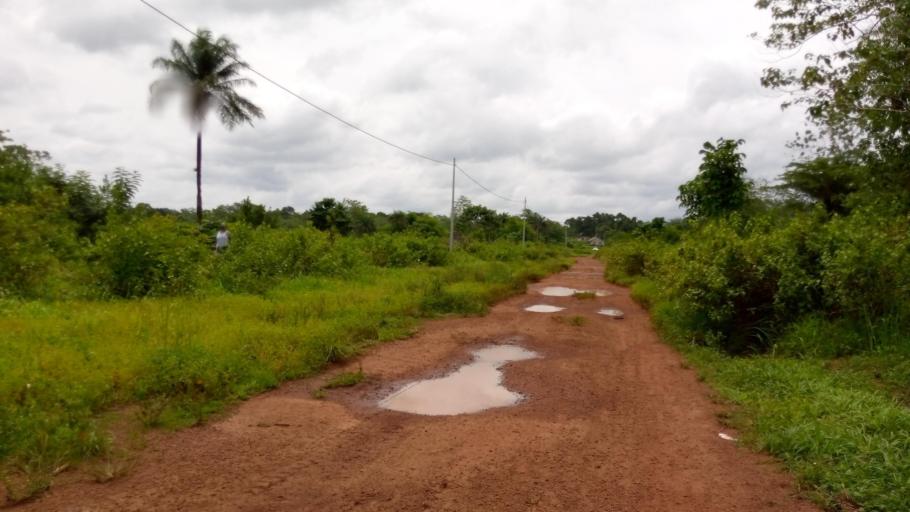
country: SL
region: Southern Province
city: Rotifunk
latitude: 8.1903
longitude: -12.5716
